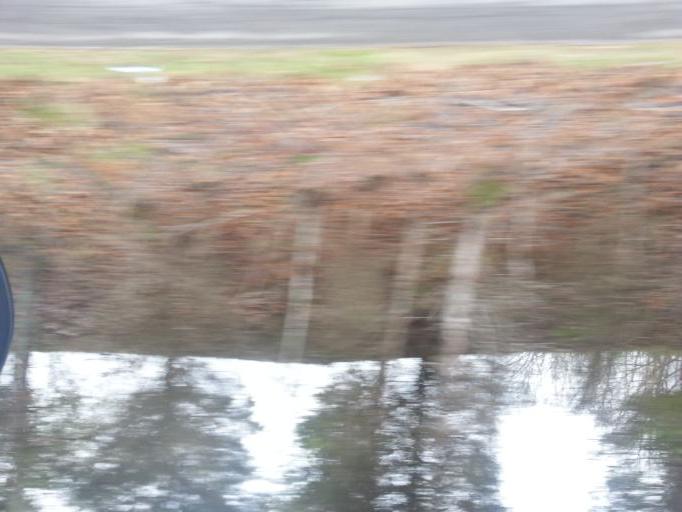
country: US
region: Tennessee
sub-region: Grainger County
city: Blaine
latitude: 36.1469
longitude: -83.6871
